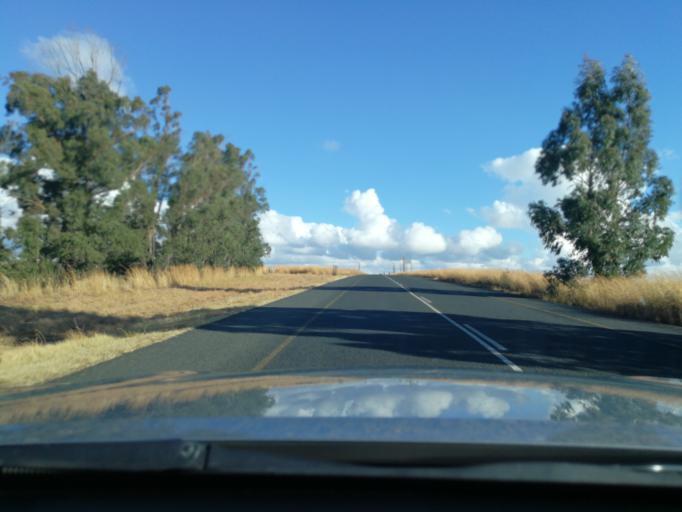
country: ZA
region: Orange Free State
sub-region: Thabo Mofutsanyana District Municipality
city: Bethlehem
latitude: -28.0648
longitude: 28.3619
